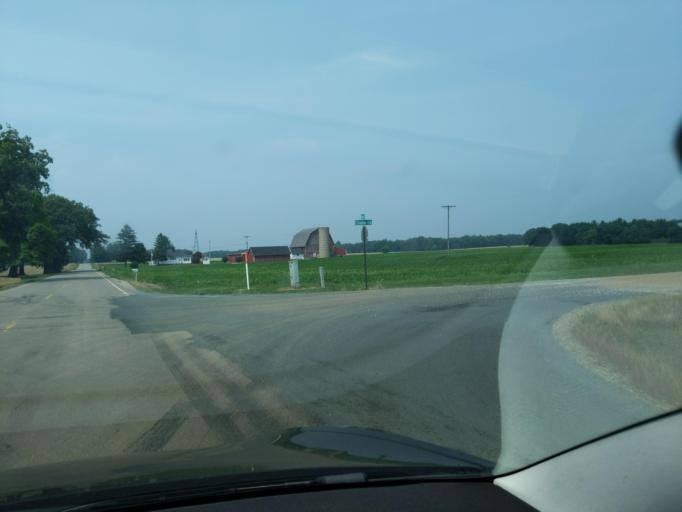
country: US
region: Michigan
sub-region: Clinton County
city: DeWitt
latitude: 42.8709
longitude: -84.5722
